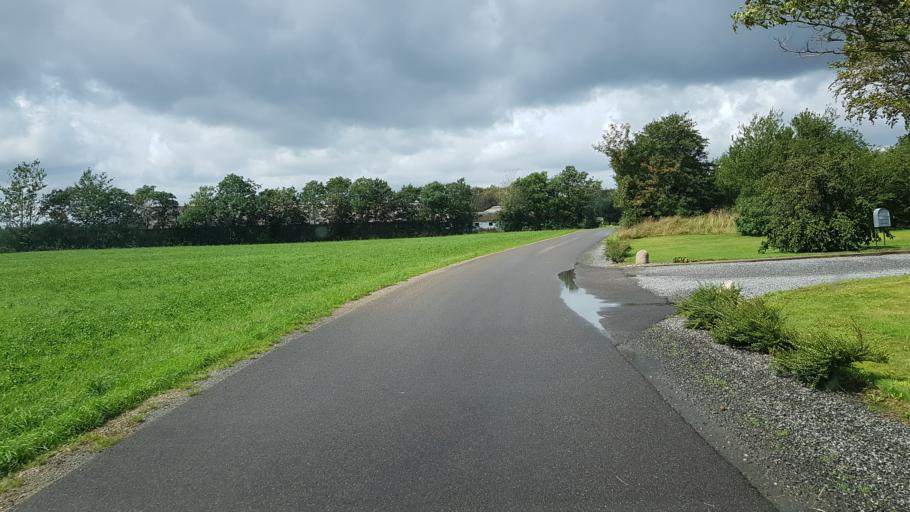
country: DK
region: South Denmark
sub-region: Vejen Kommune
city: Holsted
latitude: 55.6006
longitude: 8.8497
